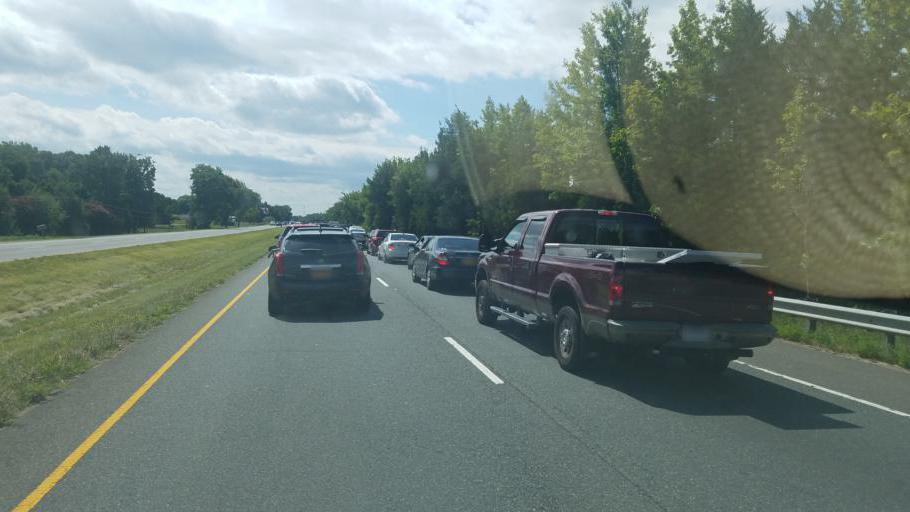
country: US
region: Virginia
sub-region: Stafford County
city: Falmouth
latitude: 38.3783
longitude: -77.5368
